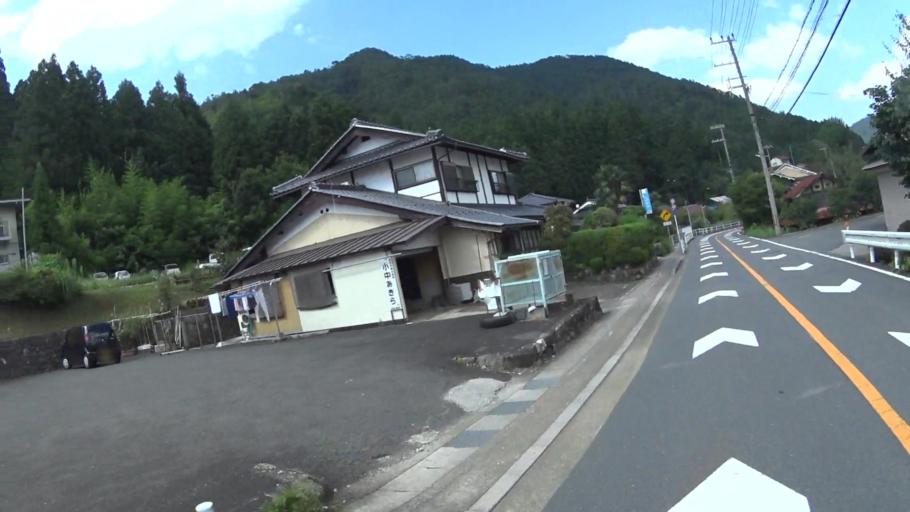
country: JP
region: Fukui
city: Obama
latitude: 35.2756
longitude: 135.5817
